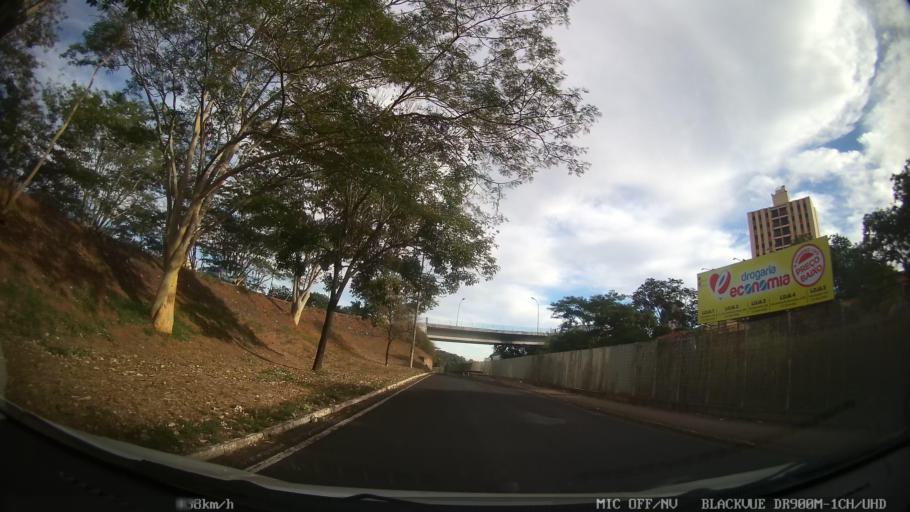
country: BR
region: Sao Paulo
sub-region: Catanduva
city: Catanduva
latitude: -21.1367
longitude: -48.9667
